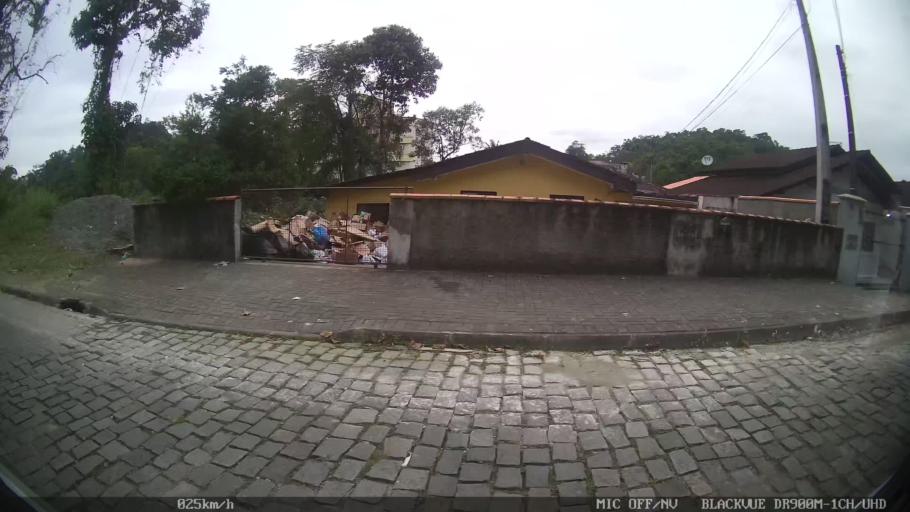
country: BR
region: Santa Catarina
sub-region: Joinville
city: Joinville
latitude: -26.2804
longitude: -48.8811
